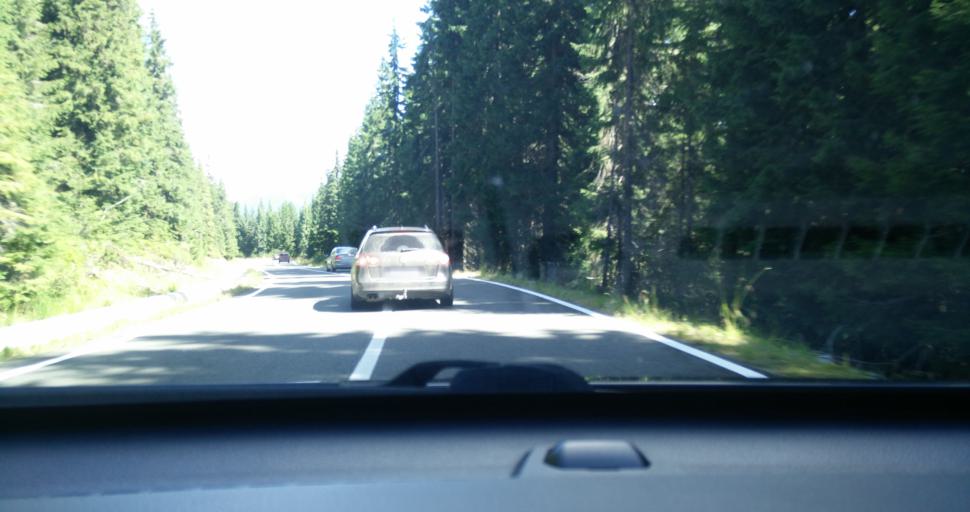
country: RO
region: Hunedoara
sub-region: Oras Petrila
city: Petrila
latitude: 45.4753
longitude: 23.6406
